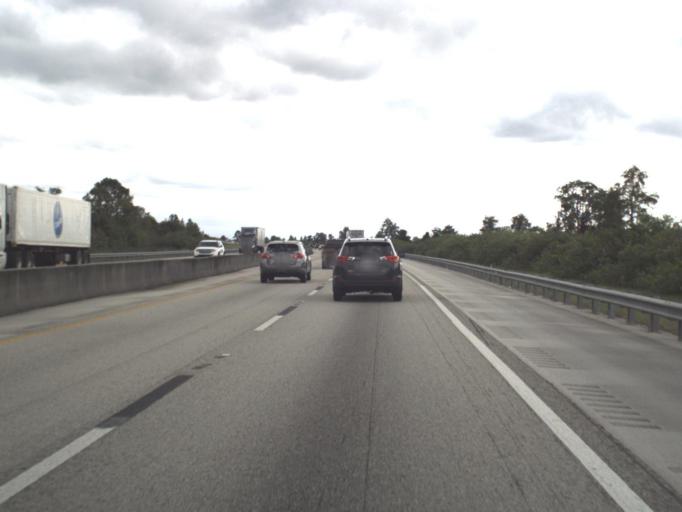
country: US
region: Florida
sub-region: Martin County
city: Hobe Sound
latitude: 27.0406
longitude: -80.2395
